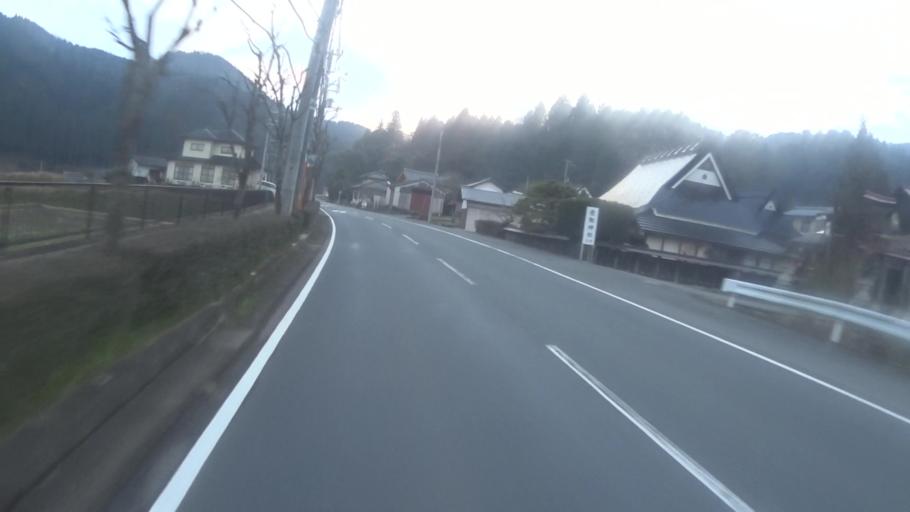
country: JP
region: Kyoto
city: Ayabe
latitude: 35.3267
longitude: 135.3323
